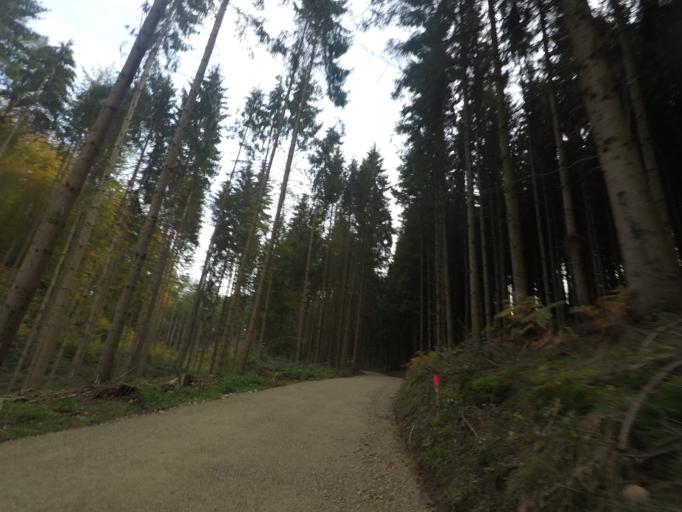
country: LU
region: Luxembourg
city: Itzig
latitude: 49.6071
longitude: 6.1873
